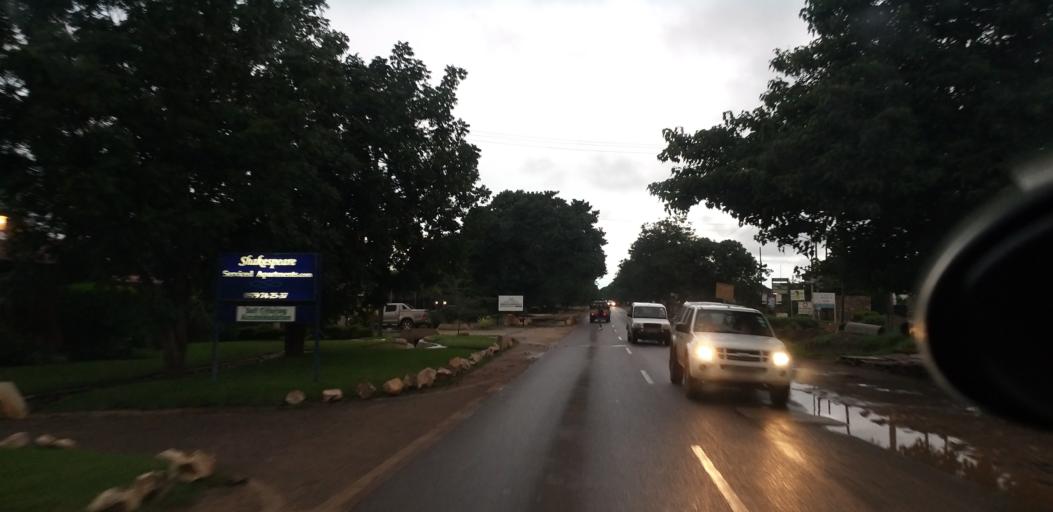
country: ZM
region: Lusaka
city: Lusaka
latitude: -15.4369
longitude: 28.3558
